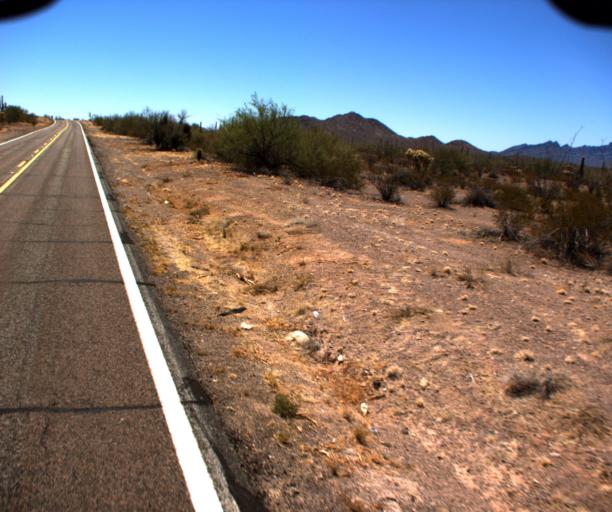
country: US
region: Arizona
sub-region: Pima County
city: Ajo
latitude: 32.2253
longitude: -112.7039
